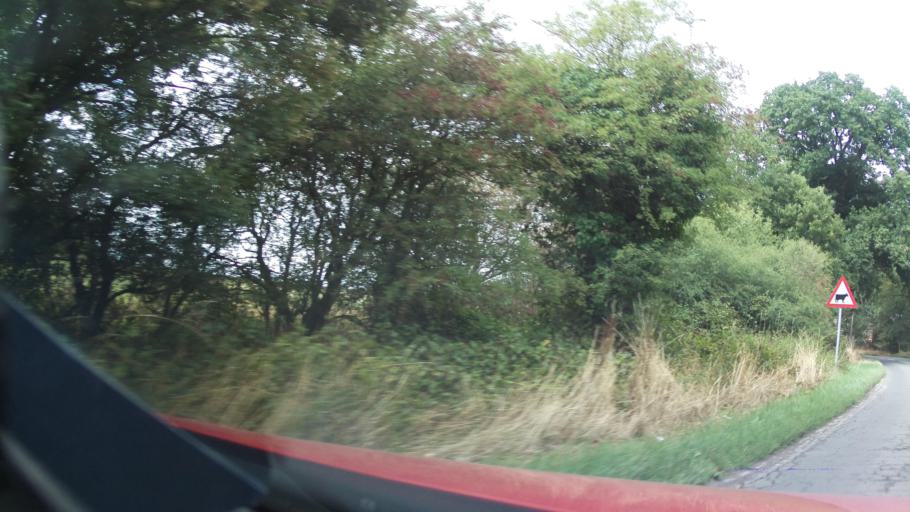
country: GB
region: England
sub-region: Nottinghamshire
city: East Leake
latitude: 52.8025
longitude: -1.1905
